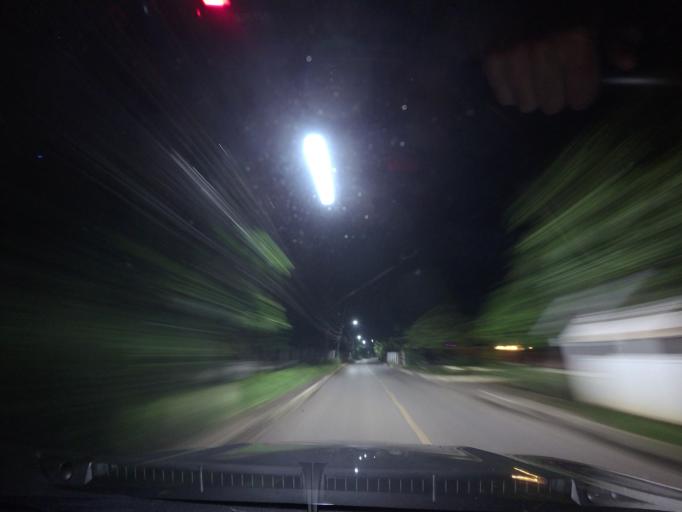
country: TH
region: Nong Khai
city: Nong Khai
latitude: 17.8734
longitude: 102.7157
